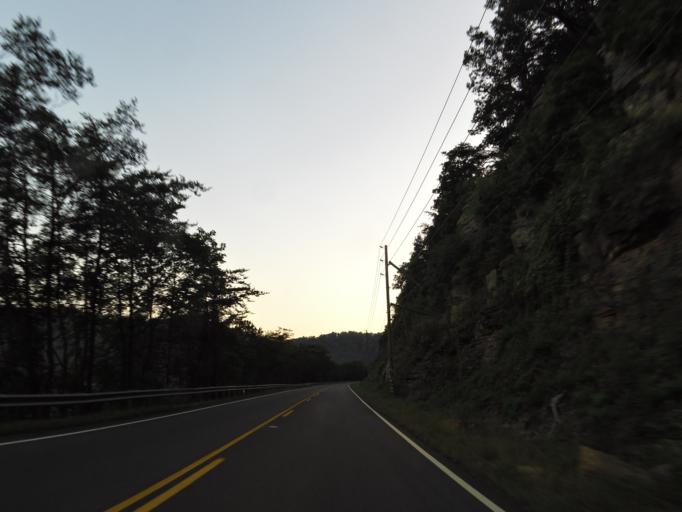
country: US
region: Tennessee
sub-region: Loudon County
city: Greenback
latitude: 35.5450
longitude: -84.0367
